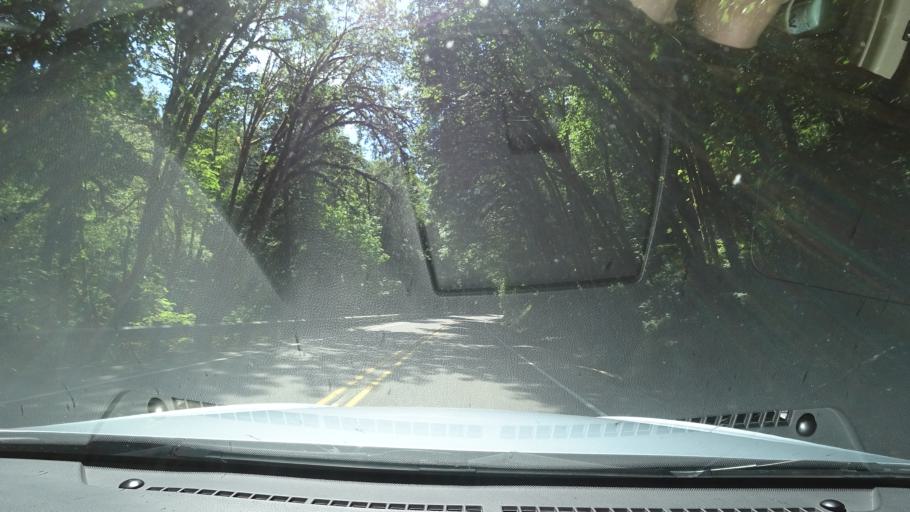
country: US
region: Oregon
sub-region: Lane County
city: Veneta
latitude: 44.0089
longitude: -123.7177
